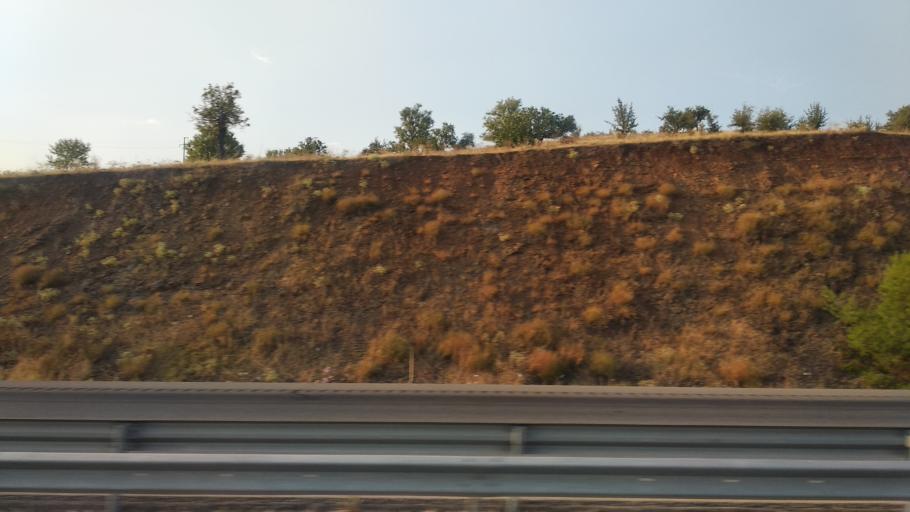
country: TR
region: Manisa
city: Menye
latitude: 38.5673
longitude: 28.5676
